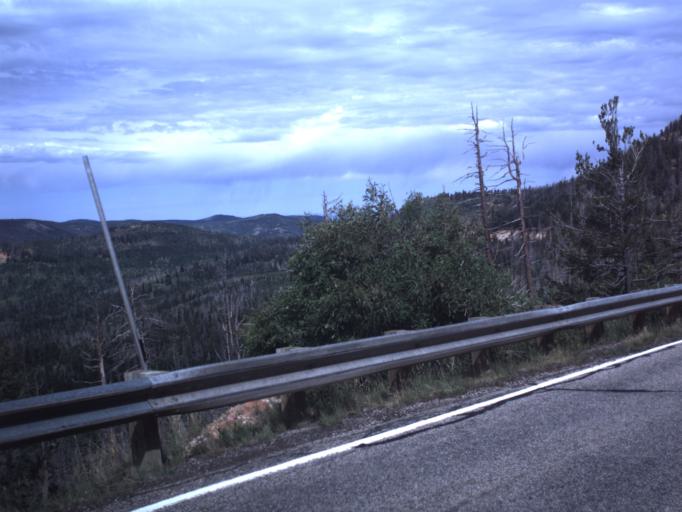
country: US
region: Utah
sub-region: Iron County
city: Cedar City
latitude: 37.5713
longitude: -112.8588
